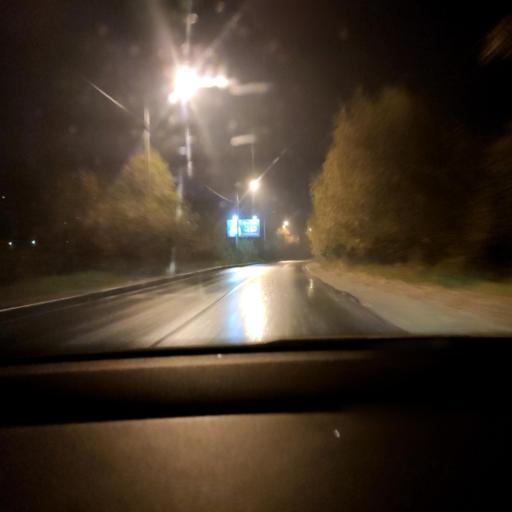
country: RU
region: Moskovskaya
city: Ivanteyevka
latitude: 55.9629
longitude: 37.9337
